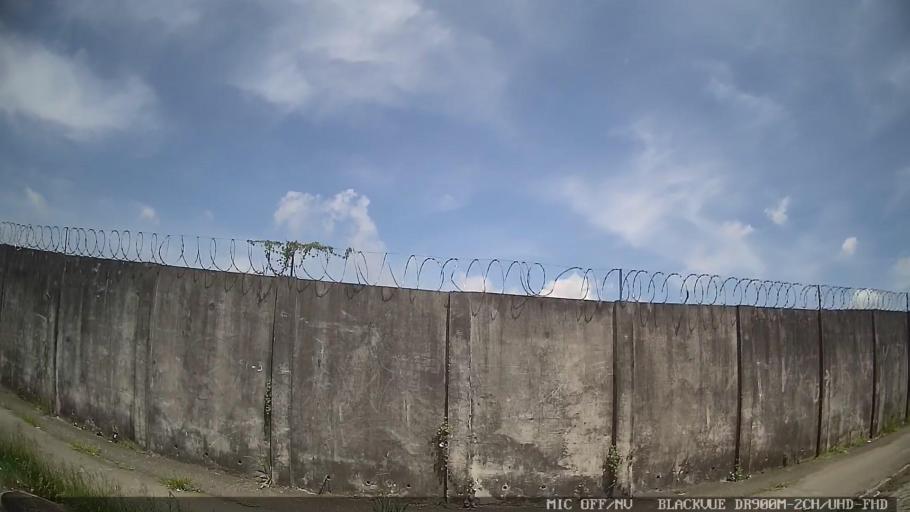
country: BR
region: Sao Paulo
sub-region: Poa
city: Poa
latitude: -23.5251
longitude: -46.3249
